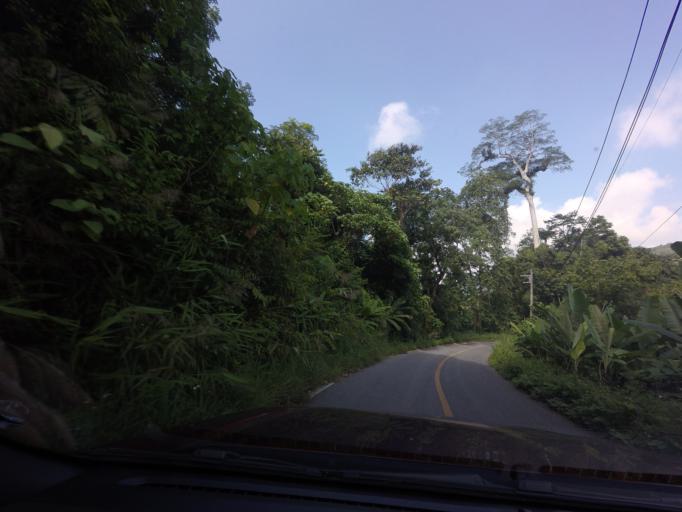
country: TH
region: Yala
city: Than To
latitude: 5.9949
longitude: 101.2132
